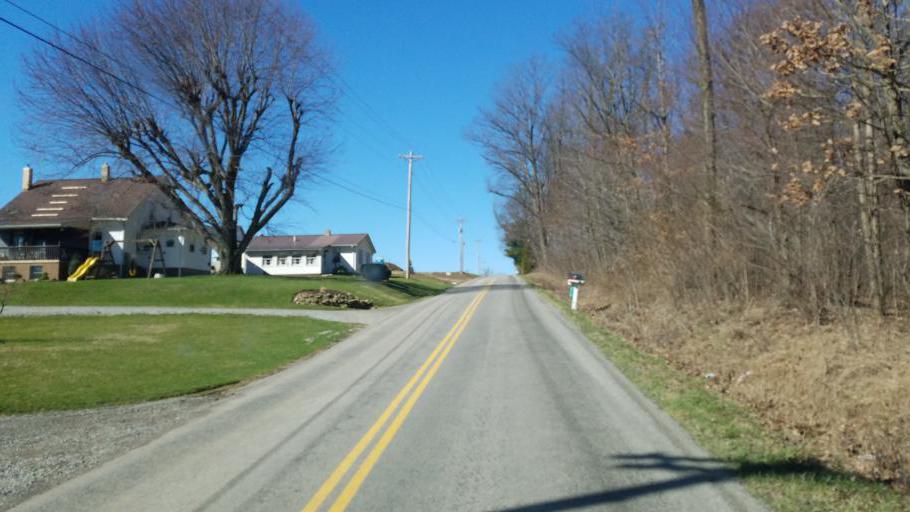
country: US
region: Ohio
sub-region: Wayne County
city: Apple Creek
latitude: 40.6533
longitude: -81.7494
